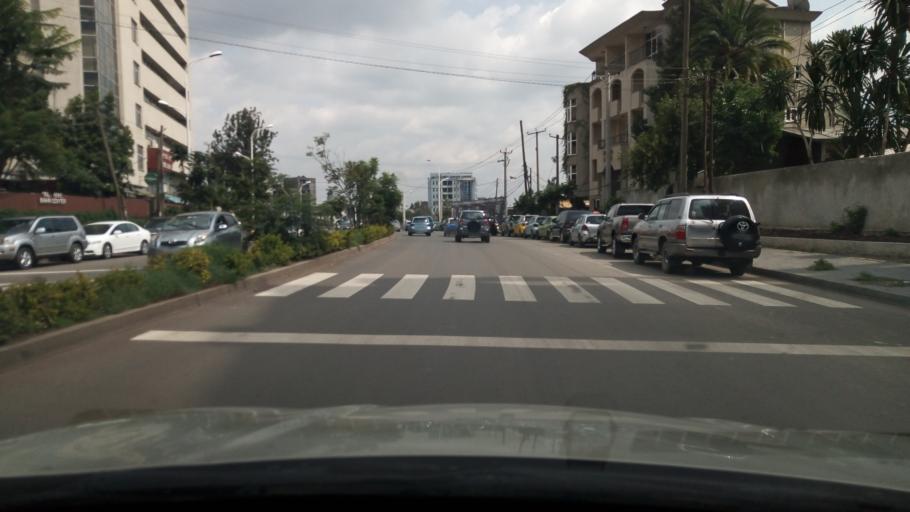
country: ET
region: Adis Abeba
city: Addis Ababa
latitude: 8.9952
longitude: 38.7785
